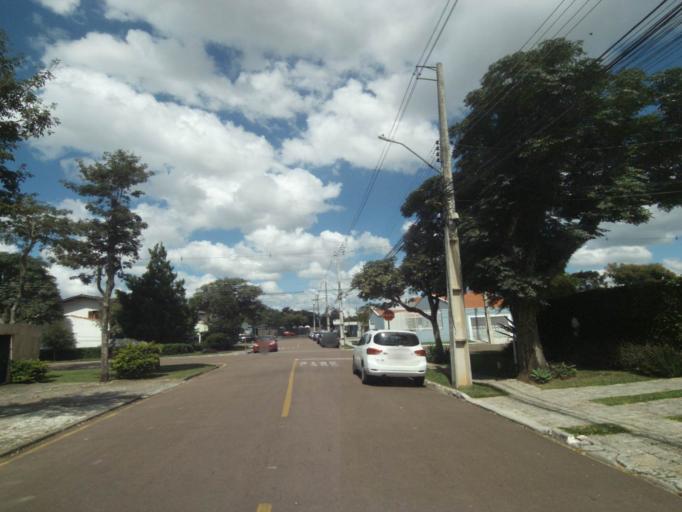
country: BR
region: Parana
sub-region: Pinhais
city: Pinhais
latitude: -25.4324
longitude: -49.2138
